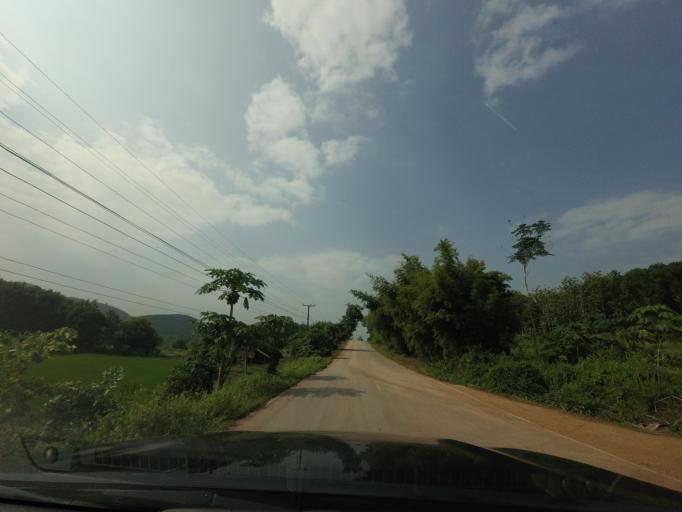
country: TH
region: Loei
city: Chiang Khan
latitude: 17.8188
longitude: 101.5663
